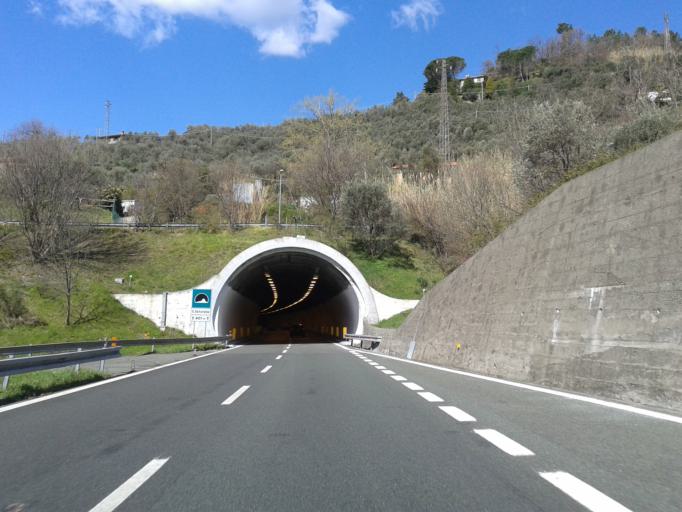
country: IT
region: Liguria
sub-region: Provincia di Genova
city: Castiglione
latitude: 44.2528
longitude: 9.5139
